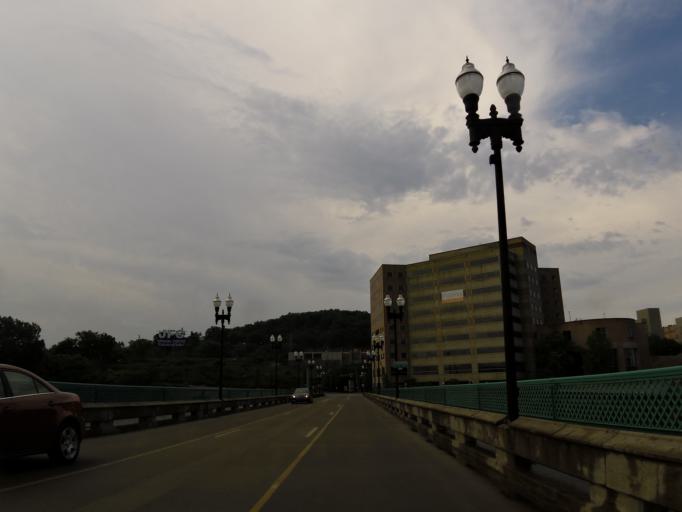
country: US
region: Tennessee
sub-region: Knox County
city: Knoxville
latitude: 35.9577
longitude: -83.9142
